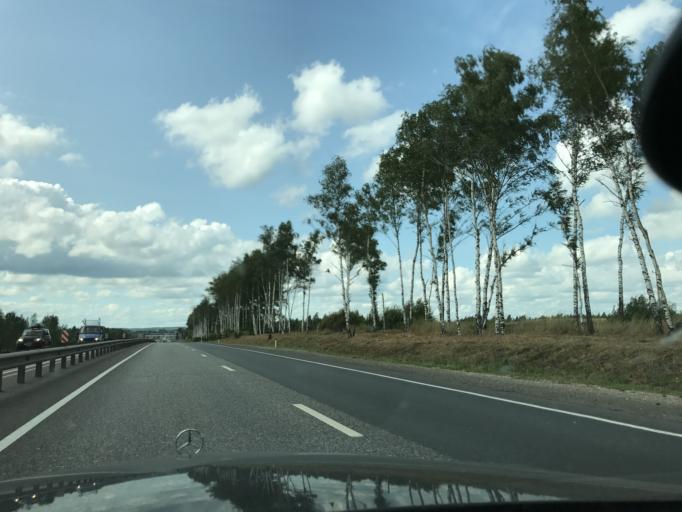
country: RU
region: Vladimir
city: Gorokhovets
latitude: 56.1652
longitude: 42.4886
